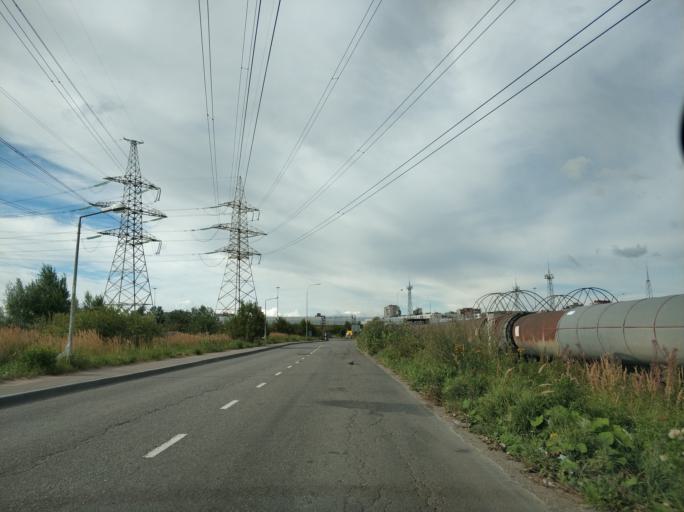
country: RU
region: Leningrad
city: Murino
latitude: 60.0466
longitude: 30.4357
